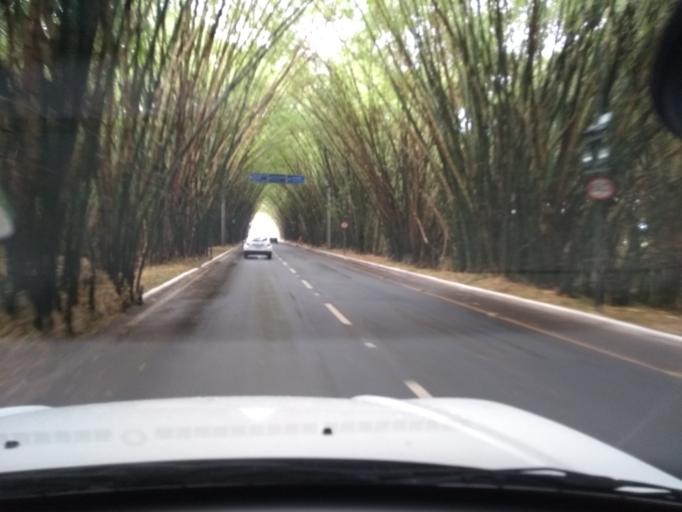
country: BR
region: Bahia
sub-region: Lauro De Freitas
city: Lauro de Freitas
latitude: -12.9087
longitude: -38.3405
